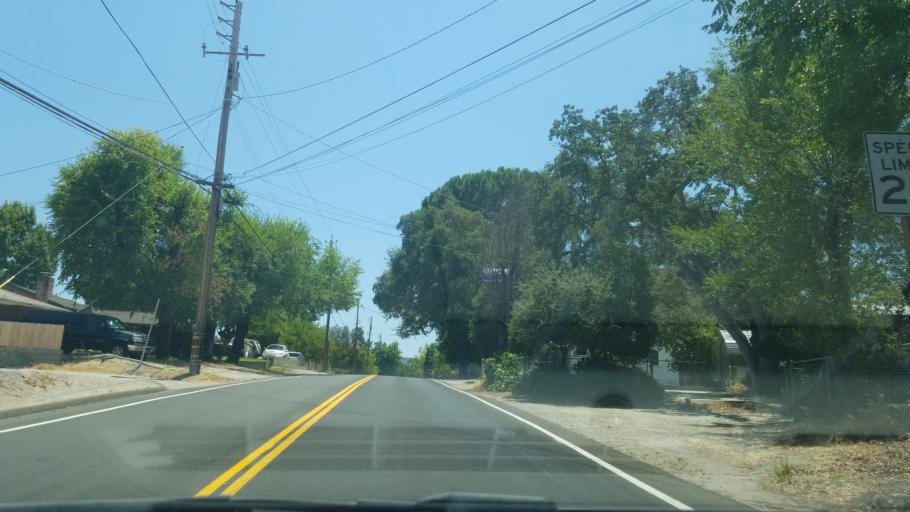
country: US
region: California
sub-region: San Luis Obispo County
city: Atascadero
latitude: 35.4815
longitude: -120.6541
